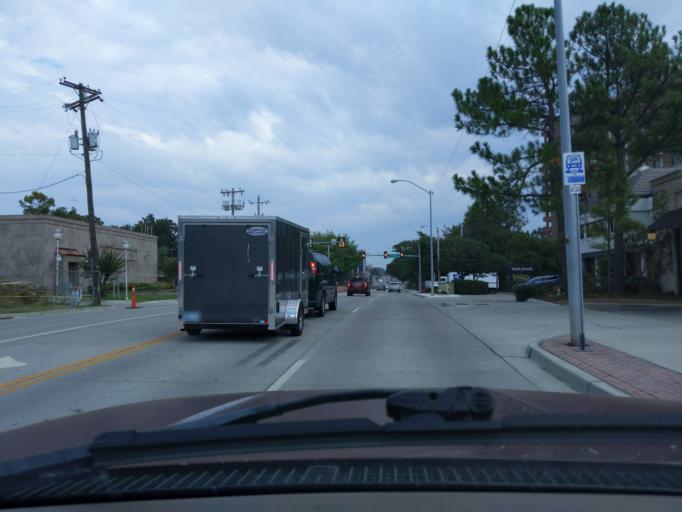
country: US
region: Oklahoma
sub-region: Tulsa County
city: Tulsa
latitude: 36.1332
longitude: -95.9630
